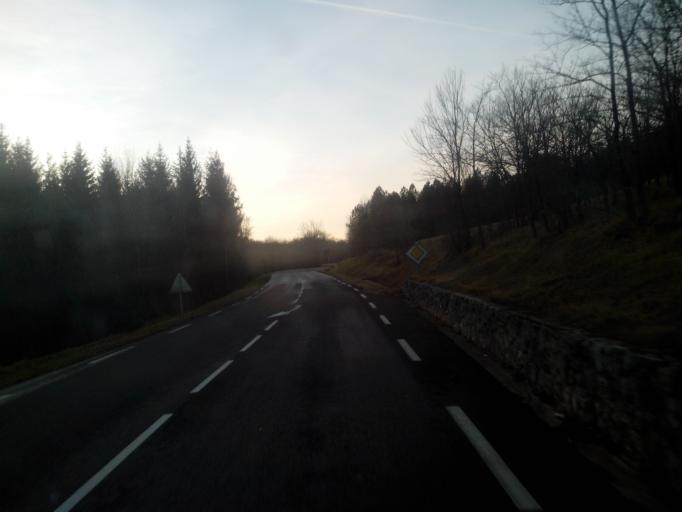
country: FR
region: Midi-Pyrenees
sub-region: Departement de l'Ariege
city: Lavelanet
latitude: 42.9195
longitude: 1.8899
